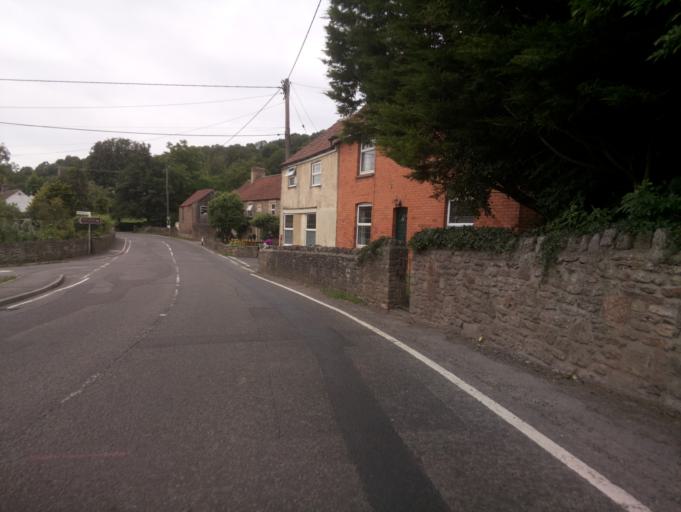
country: GB
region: England
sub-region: Somerset
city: Bradley Cross
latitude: 51.2478
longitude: -2.7367
